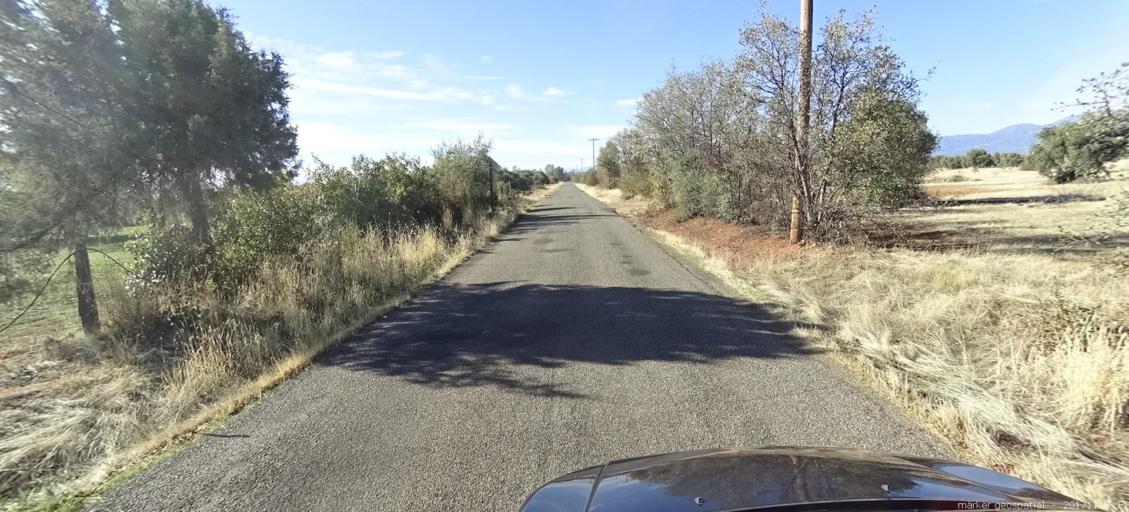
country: US
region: California
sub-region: Shasta County
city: Anderson
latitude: 40.4392
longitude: -122.4283
